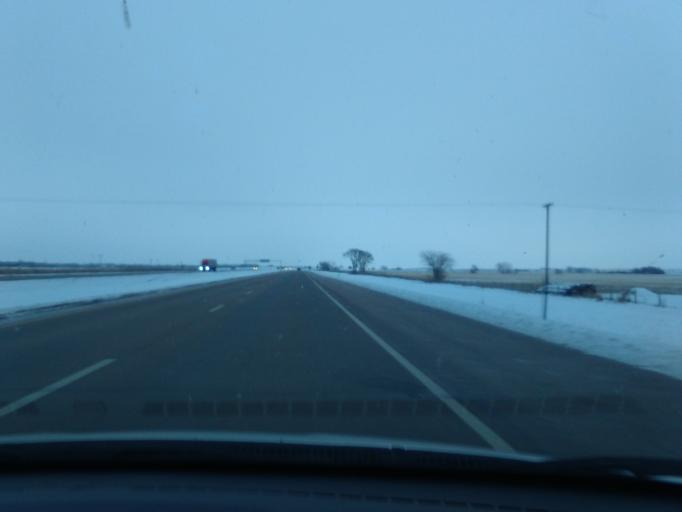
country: US
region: Nebraska
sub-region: Keith County
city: Ogallala
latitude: 41.1204
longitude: -101.6735
